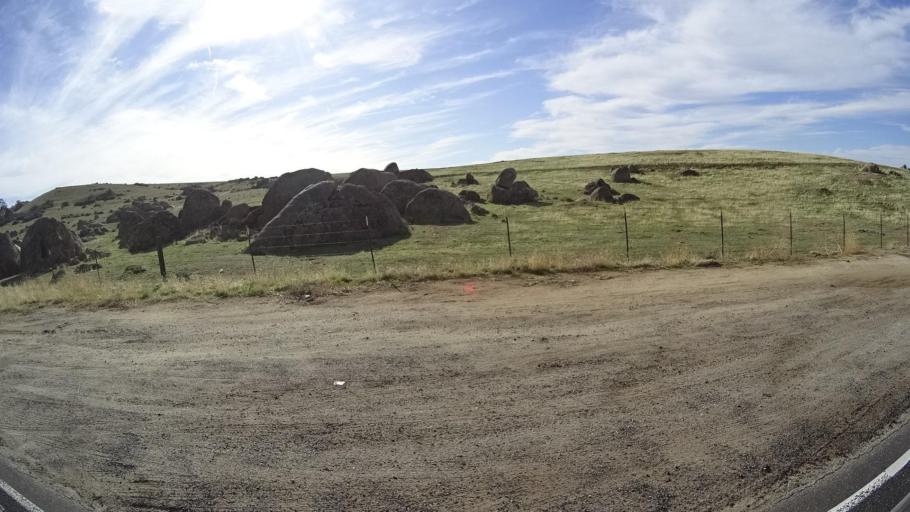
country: US
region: California
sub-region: Kern County
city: Oildale
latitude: 35.6126
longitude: -118.8611
